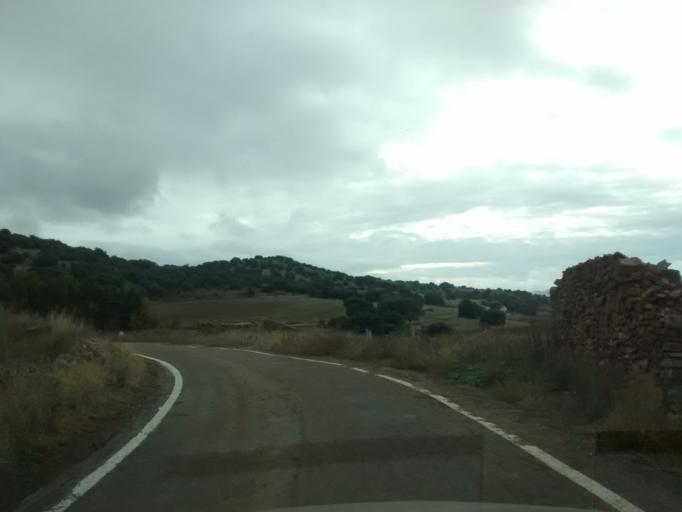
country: ES
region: Aragon
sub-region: Provincia de Teruel
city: Castejon de Tornos
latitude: 40.9892
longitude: -1.4677
